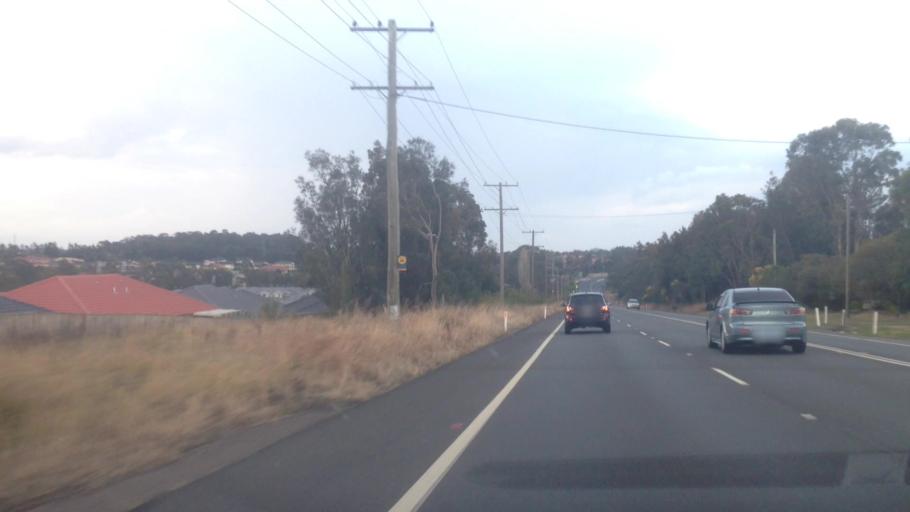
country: AU
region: New South Wales
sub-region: Wyong Shire
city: Kanwal
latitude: -33.2584
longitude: 151.4855
